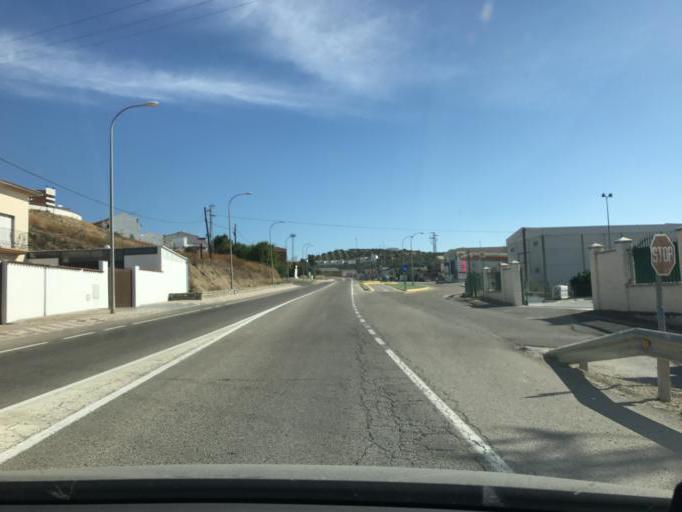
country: ES
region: Andalusia
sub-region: Province of Cordoba
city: Espejo
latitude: 37.6744
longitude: -4.5571
